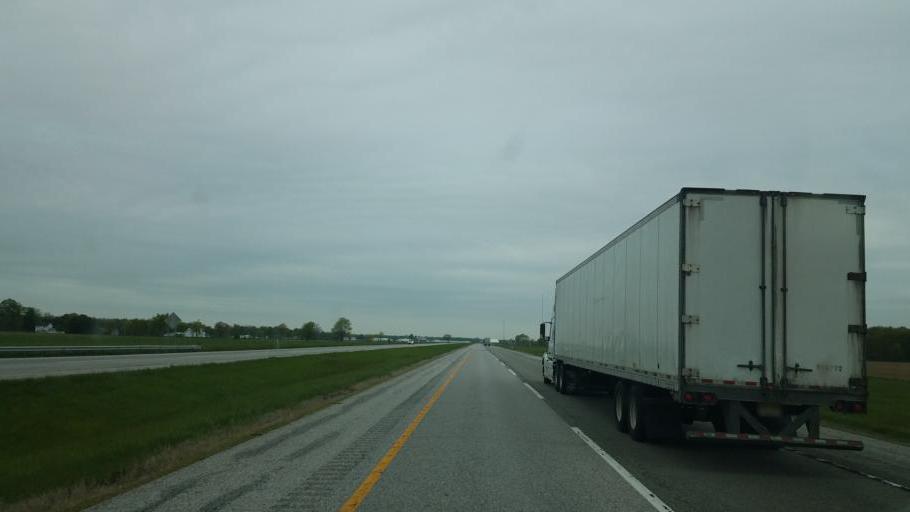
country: US
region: Michigan
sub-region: Saint Joseph County
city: Sturgis
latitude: 41.7457
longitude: -85.5154
